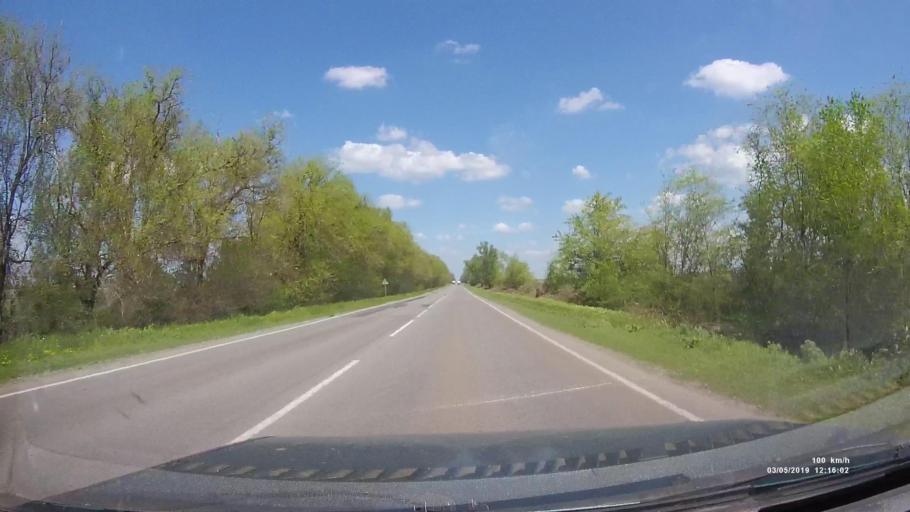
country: RU
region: Rostov
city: Melikhovskaya
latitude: 47.3661
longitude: 40.5799
